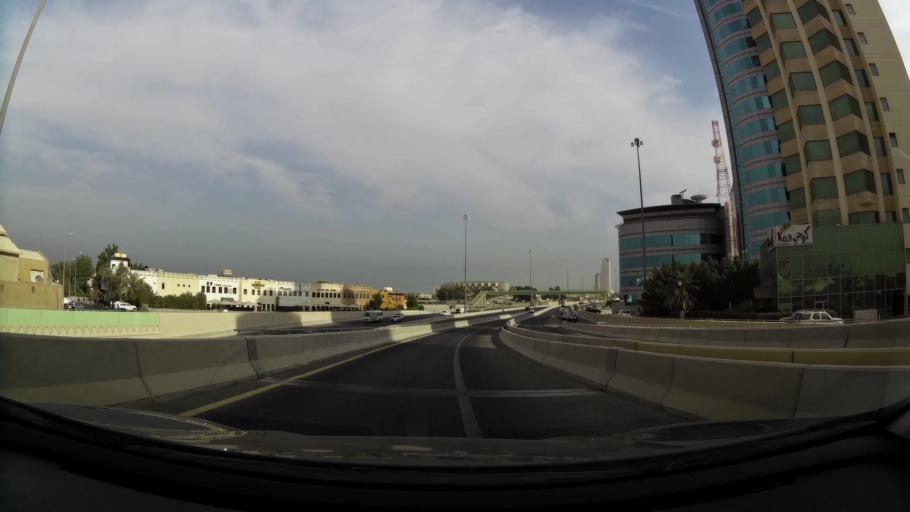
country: KW
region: Al Asimah
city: Ash Shamiyah
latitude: 29.3634
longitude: 47.9607
